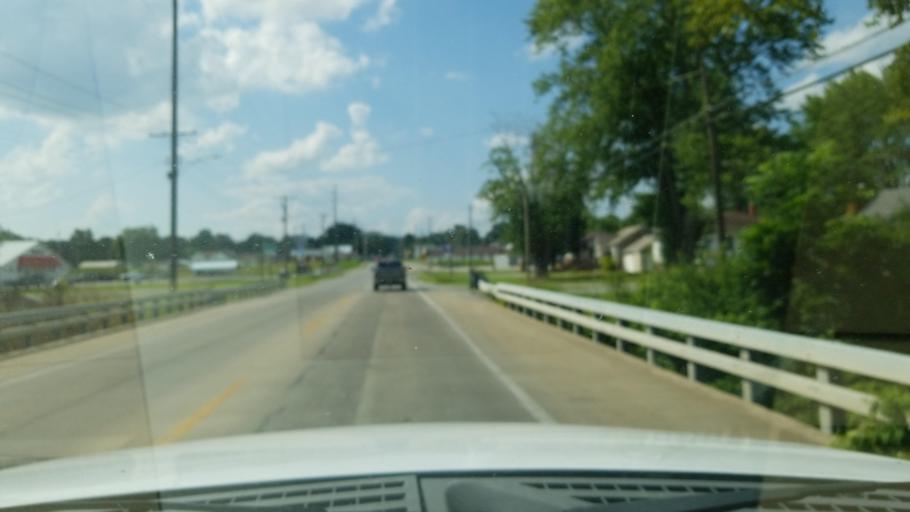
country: US
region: Illinois
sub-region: Saline County
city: Eldorado
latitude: 37.8078
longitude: -88.4421
